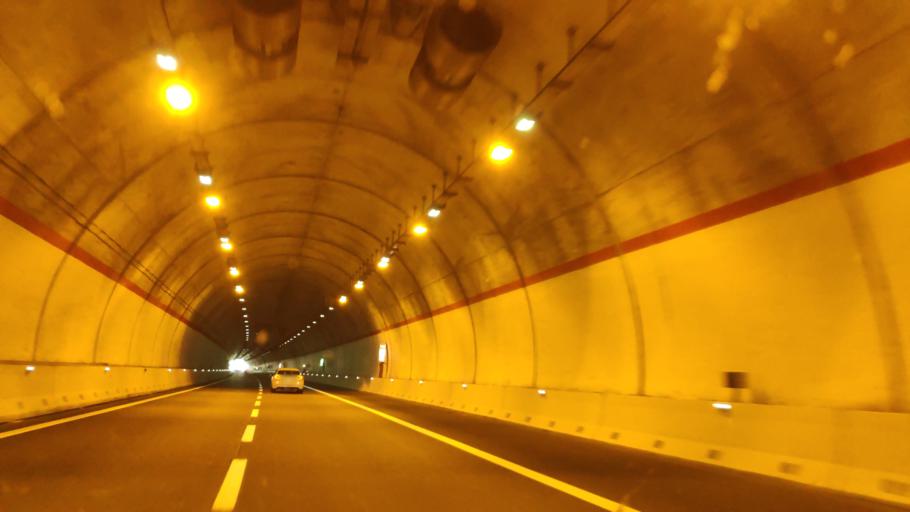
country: IT
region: Campania
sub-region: Provincia di Salerno
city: Buonabitacolo
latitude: 40.2554
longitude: 15.6604
